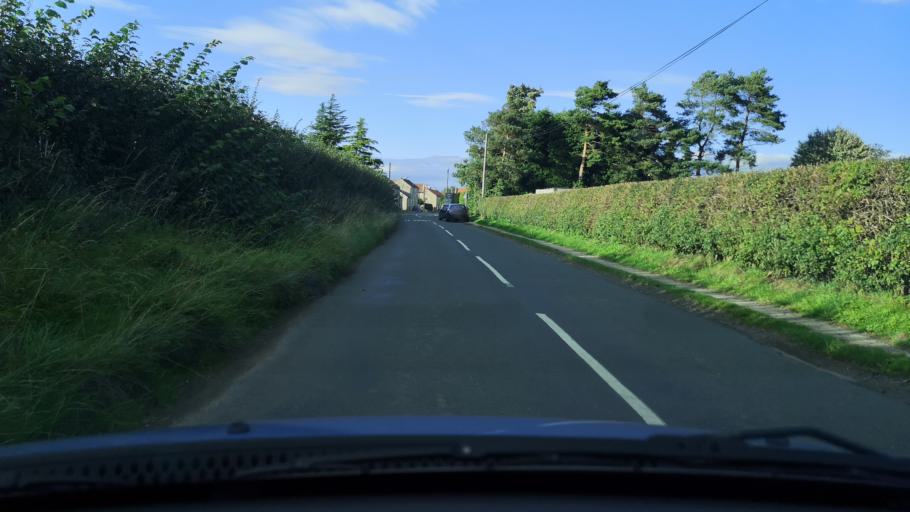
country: GB
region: England
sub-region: Doncaster
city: Norton
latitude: 53.6409
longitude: -1.2186
